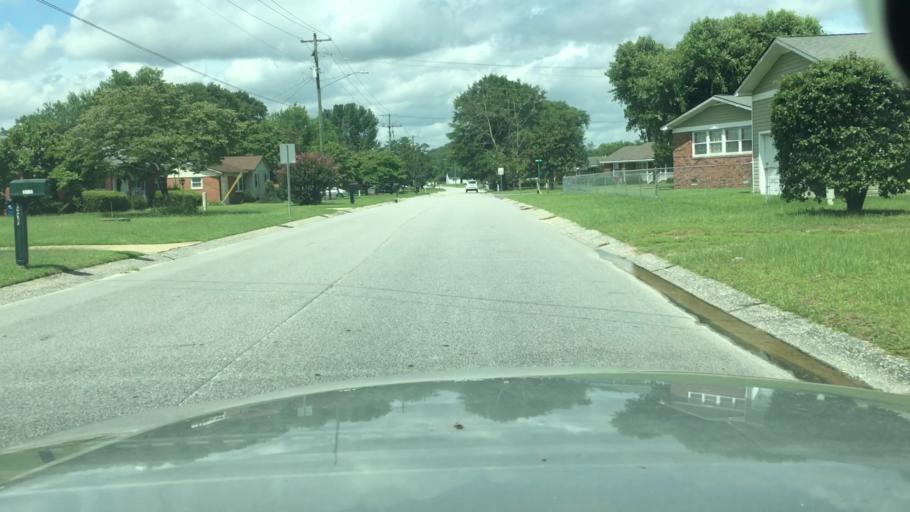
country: US
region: North Carolina
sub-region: Cumberland County
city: Hope Mills
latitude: 35.0326
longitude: -78.9933
